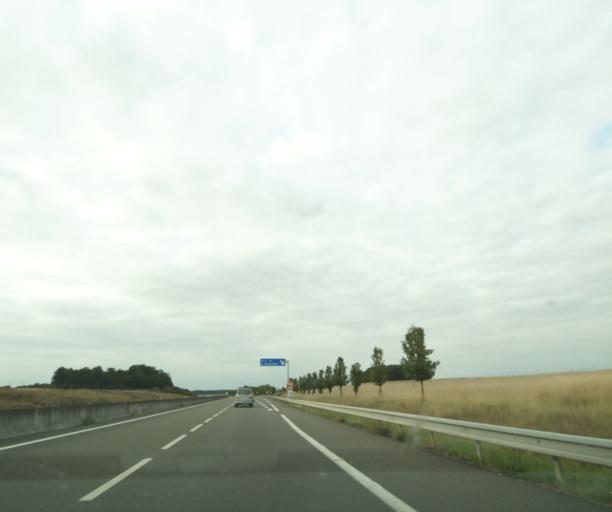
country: FR
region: Centre
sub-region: Departement d'Indre-et-Loire
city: Rouziers-de-Touraine
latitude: 47.5326
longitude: 0.6200
